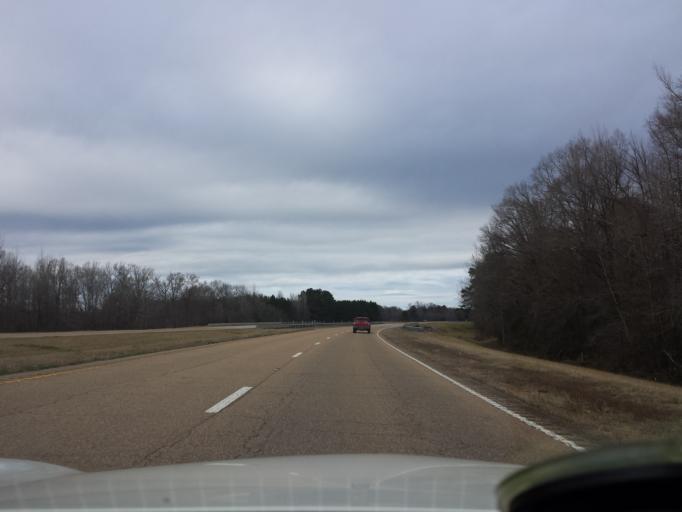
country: US
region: Mississippi
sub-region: Oktibbeha County
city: Starkville
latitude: 33.2943
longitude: -88.9060
